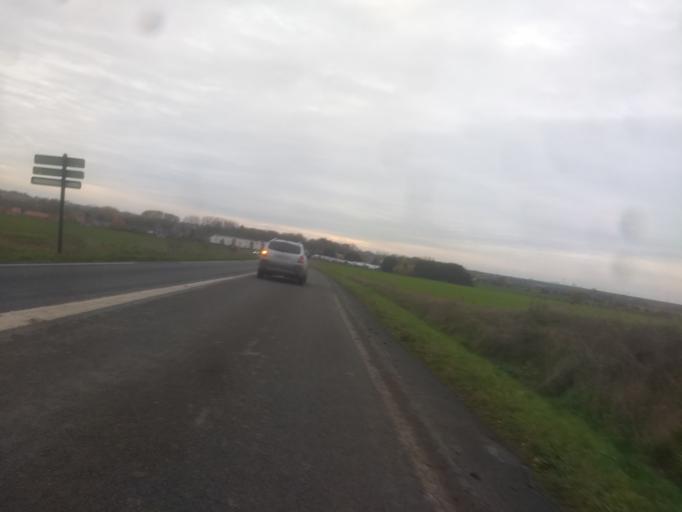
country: FR
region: Nord-Pas-de-Calais
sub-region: Departement du Pas-de-Calais
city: Achicourt
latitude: 50.2704
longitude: 2.7466
